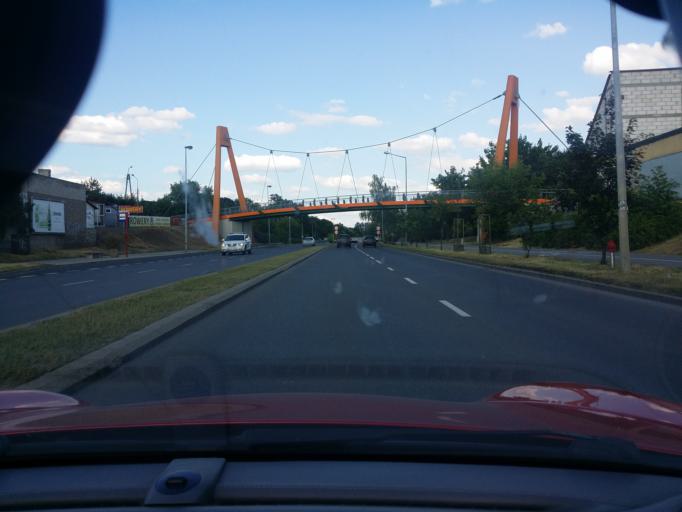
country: PL
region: Masovian Voivodeship
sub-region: Radom
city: Radom
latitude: 51.4136
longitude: 21.1493
